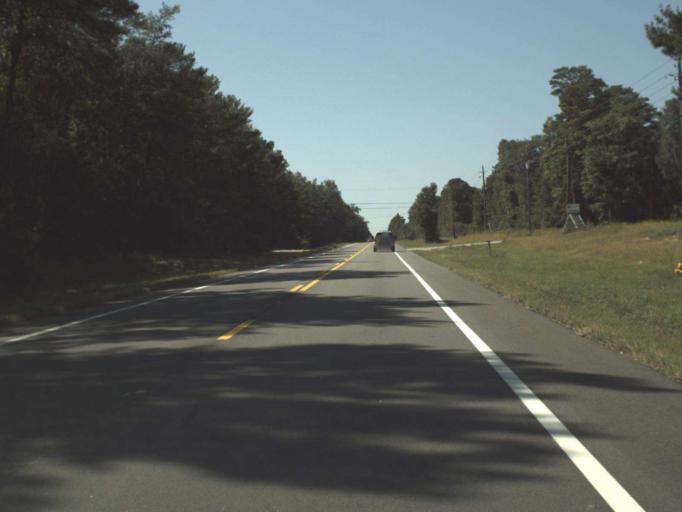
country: US
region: Florida
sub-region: Walton County
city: Miramar Beach
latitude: 30.4823
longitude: -86.2894
